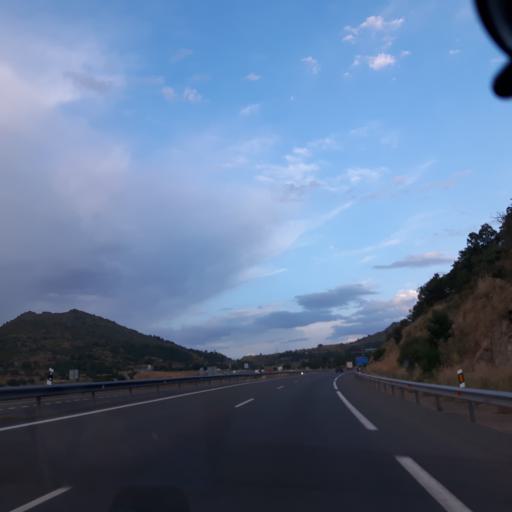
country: ES
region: Castille and Leon
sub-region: Provincia de Salamanca
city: Sorihuela
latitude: 40.4415
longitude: -5.6890
